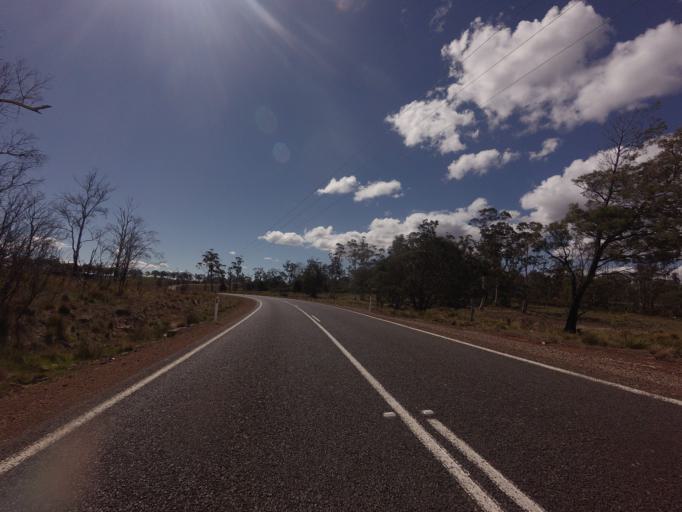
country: AU
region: Tasmania
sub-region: Northern Midlands
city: Evandale
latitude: -41.9528
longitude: 147.6110
